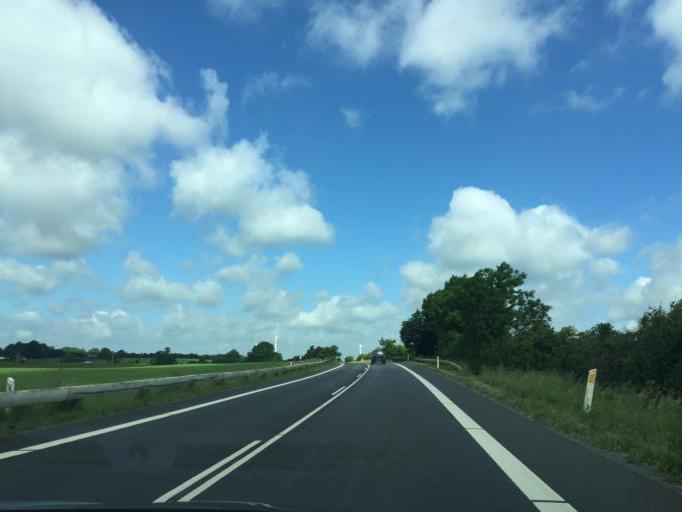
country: DK
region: South Denmark
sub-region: Middelfart Kommune
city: Brenderup
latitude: 55.4486
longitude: 9.9794
